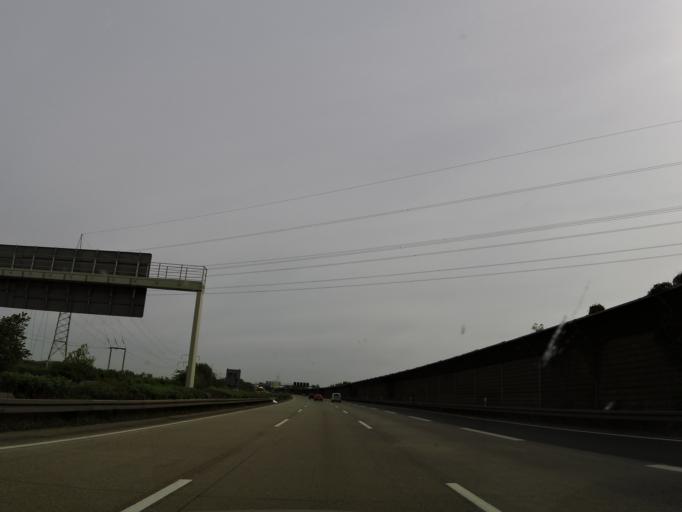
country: DE
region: Lower Saxony
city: Lehrte
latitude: 52.3646
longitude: 9.8914
